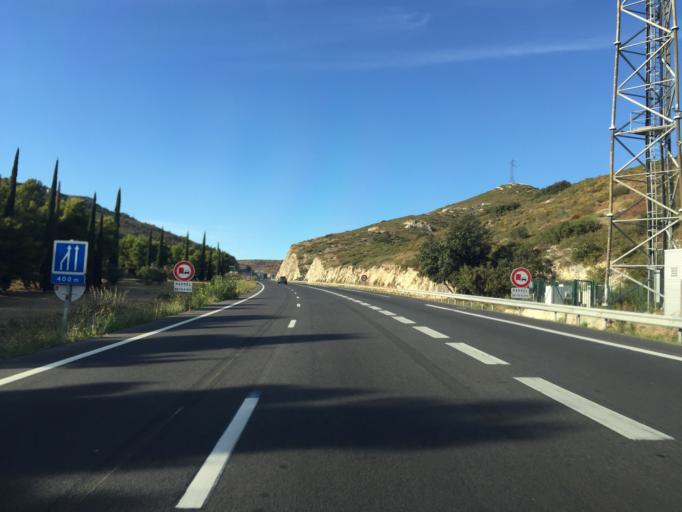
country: FR
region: Provence-Alpes-Cote d'Azur
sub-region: Departement des Bouches-du-Rhone
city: Coudoux
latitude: 43.5573
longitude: 5.2311
